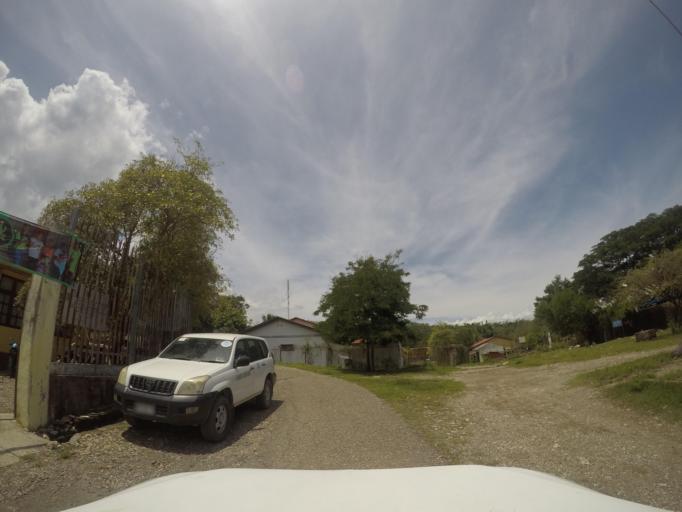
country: TL
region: Bobonaro
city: Maliana
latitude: -8.9963
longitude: 125.2248
